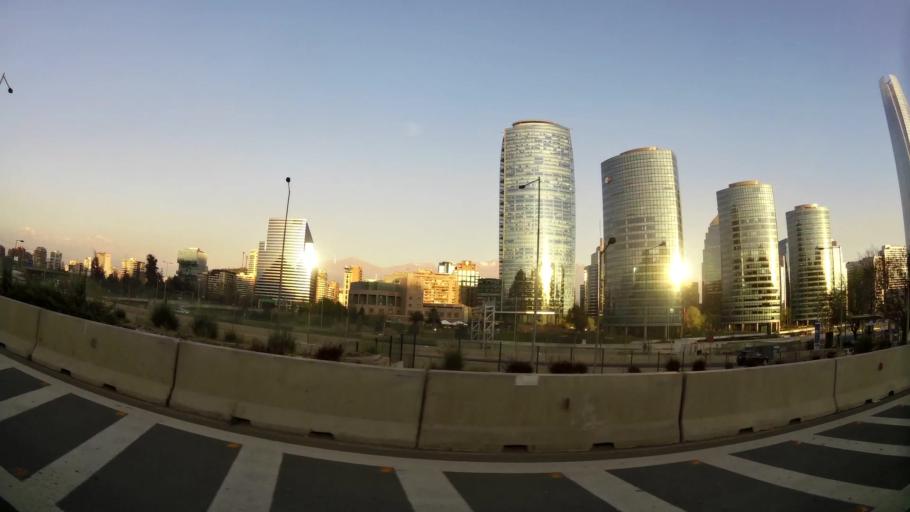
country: CL
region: Santiago Metropolitan
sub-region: Provincia de Santiago
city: Villa Presidente Frei, Nunoa, Santiago, Chile
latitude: -33.4114
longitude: -70.6077
